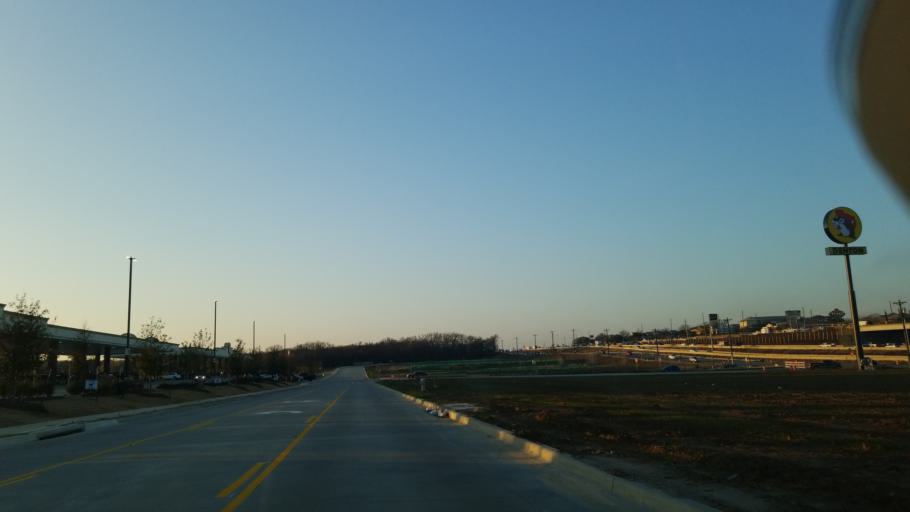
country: US
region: Texas
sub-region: Denton County
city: Corinth
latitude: 33.1792
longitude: -97.1007
